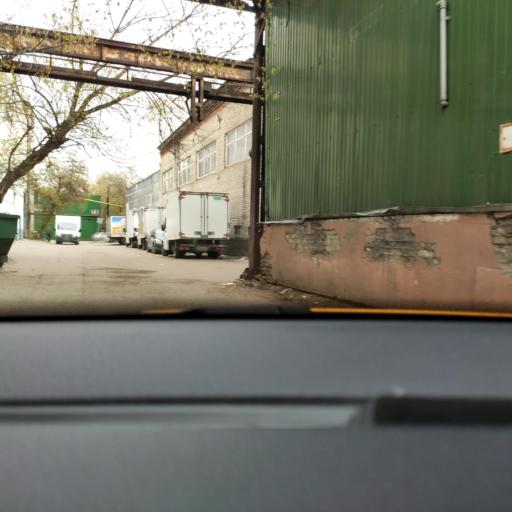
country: RU
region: Moscow
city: Lefortovo
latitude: 55.7390
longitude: 37.7083
